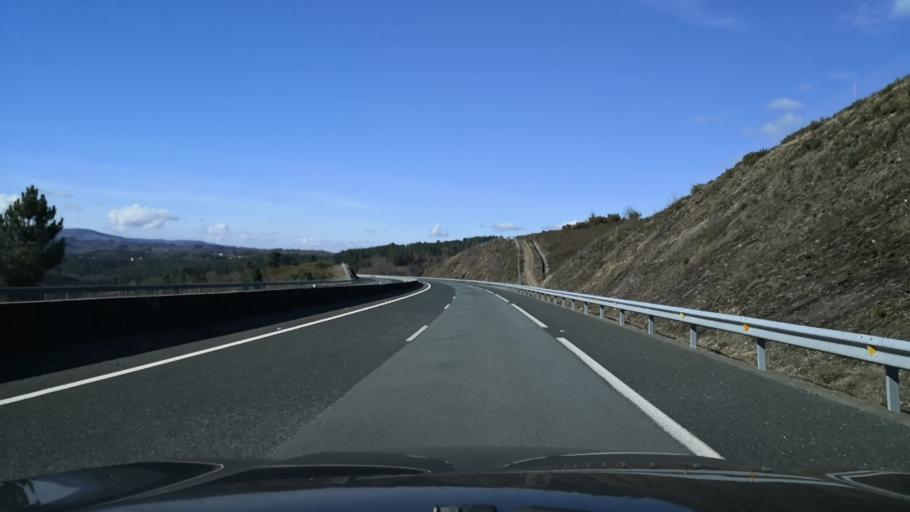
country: ES
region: Galicia
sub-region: Provincia de Pontevedra
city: Lalin
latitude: 42.5969
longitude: -8.0875
